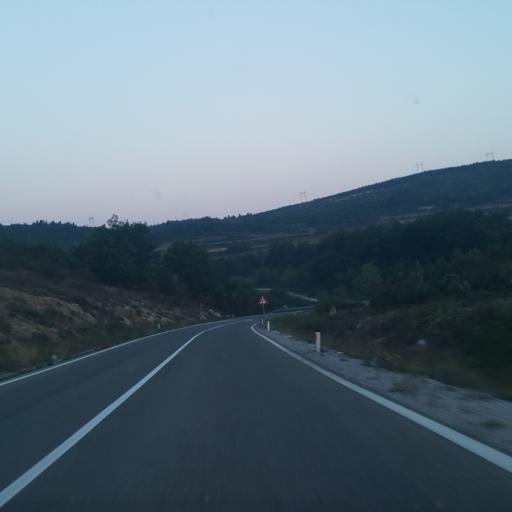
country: RS
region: Central Serbia
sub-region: Nisavski Okrug
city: Svrljig
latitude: 43.4529
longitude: 22.1794
